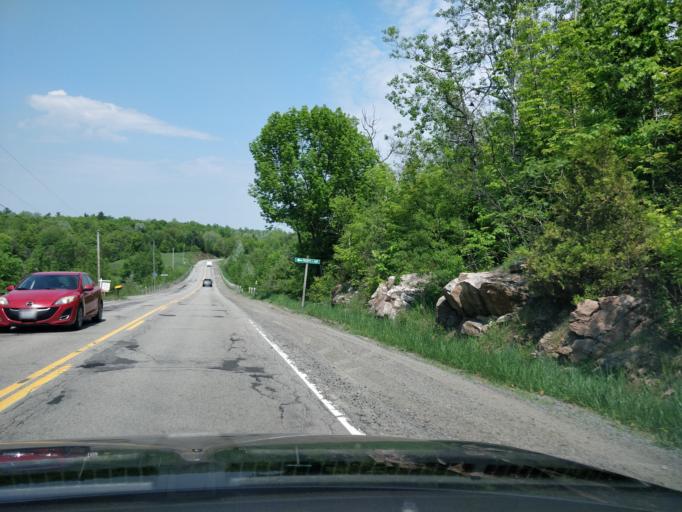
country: CA
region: Ontario
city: Perth
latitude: 44.7537
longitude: -76.3897
